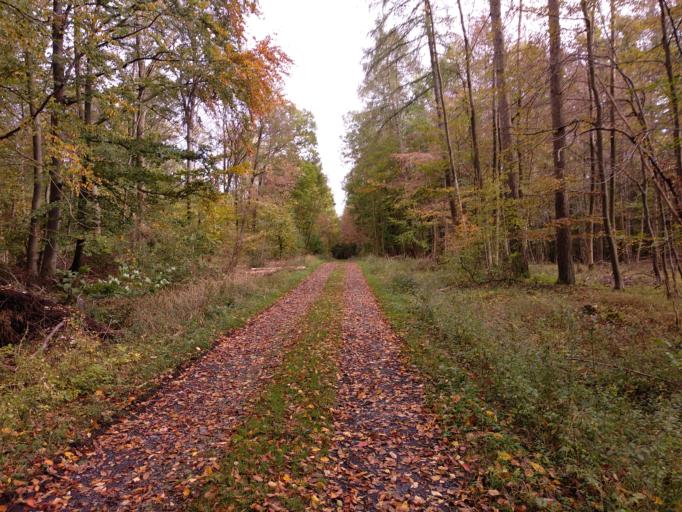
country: DE
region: North Rhine-Westphalia
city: Beverungen
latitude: 51.6636
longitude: 9.3410
